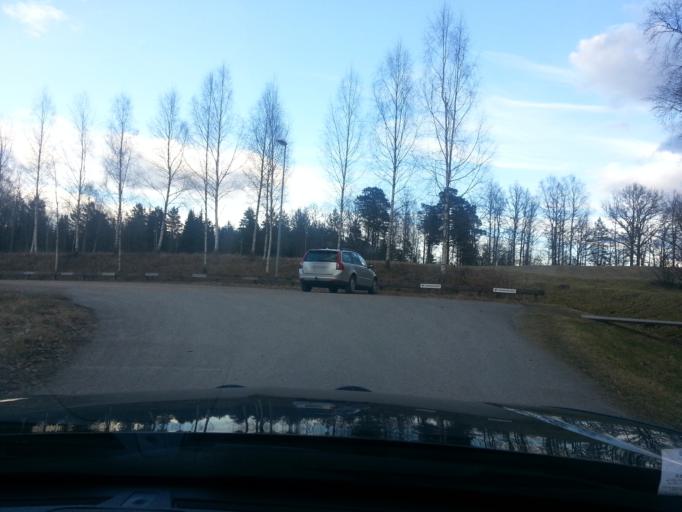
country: SE
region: Joenkoeping
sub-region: Vetlanda Kommun
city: Vetlanda
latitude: 57.4099
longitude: 15.0470
